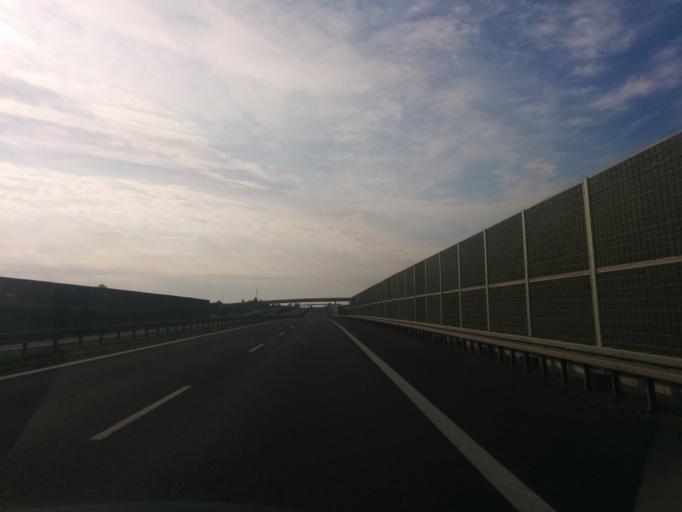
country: PL
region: Masovian Voivodeship
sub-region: Powiat grojecki
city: Jasieniec
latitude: 51.7910
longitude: 20.8922
